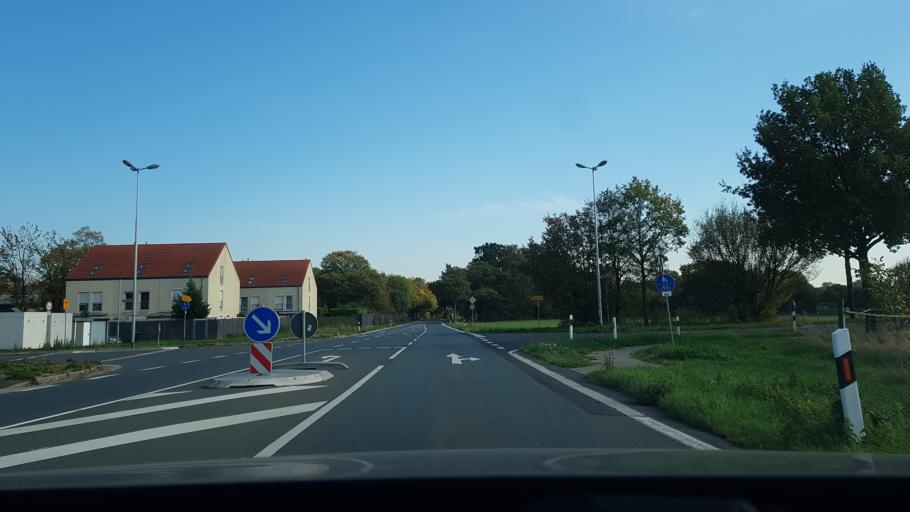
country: DE
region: North Rhine-Westphalia
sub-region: Regierungsbezirk Dusseldorf
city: Moers
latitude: 51.4459
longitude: 6.6045
